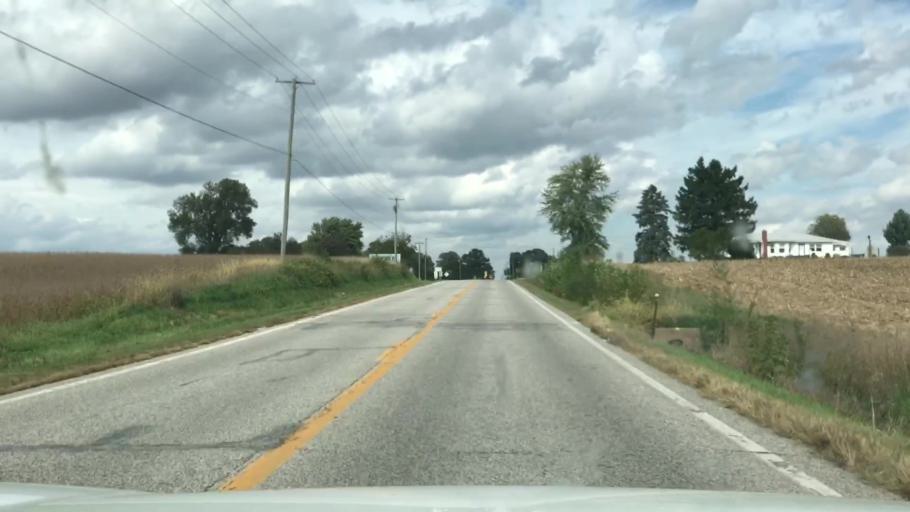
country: US
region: Illinois
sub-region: Adams County
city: Quincy
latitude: 39.9994
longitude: -91.3770
